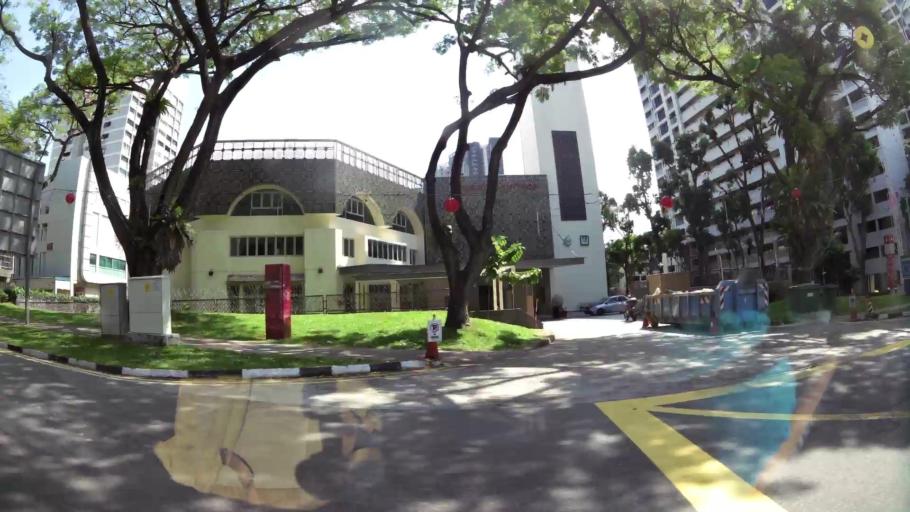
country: SG
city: Singapore
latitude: 1.3703
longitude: 103.8456
